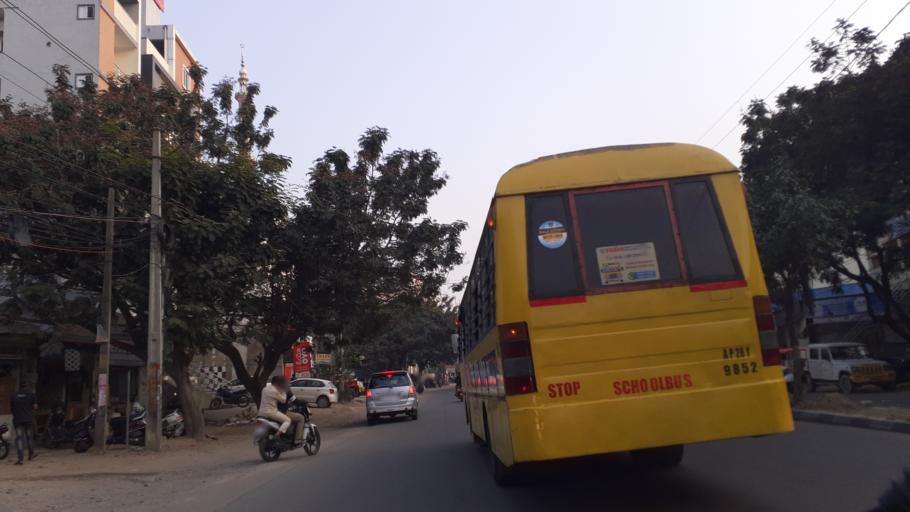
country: IN
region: Telangana
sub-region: Rangareddi
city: Kukatpalli
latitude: 17.4774
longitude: 78.3625
